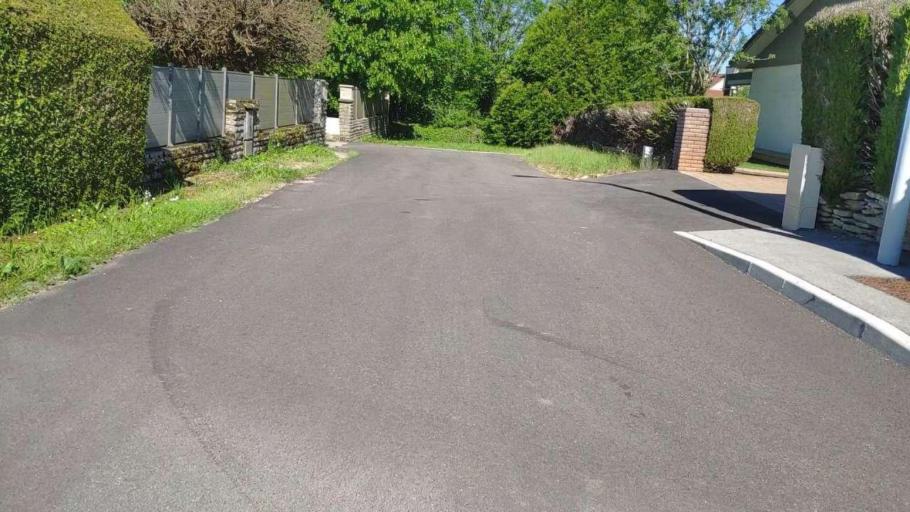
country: FR
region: Franche-Comte
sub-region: Departement du Jura
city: Perrigny
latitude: 46.6872
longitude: 5.6651
